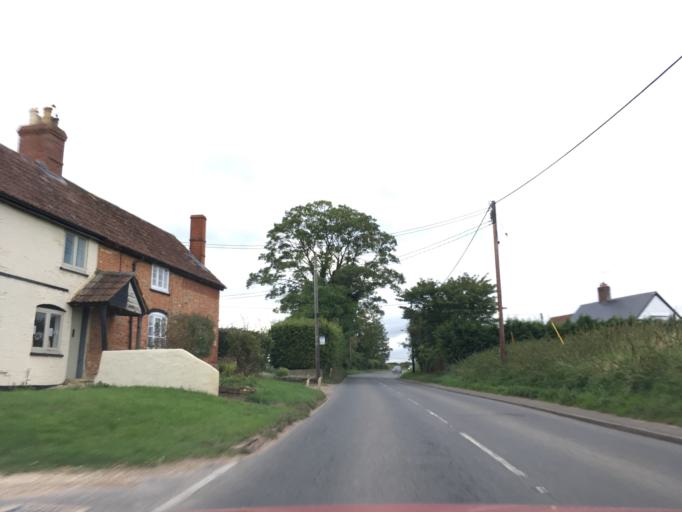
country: GB
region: England
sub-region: Wiltshire
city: Devizes
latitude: 51.3806
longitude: -2.0354
